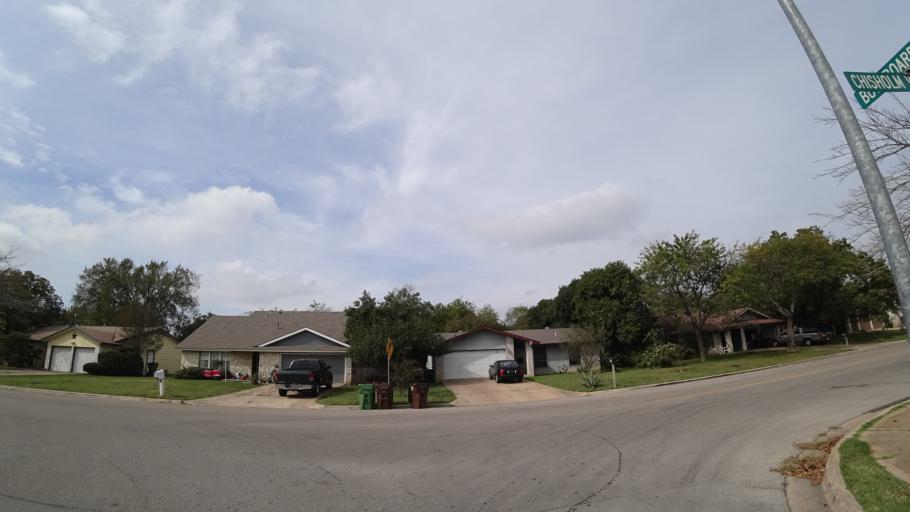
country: US
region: Texas
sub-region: Williamson County
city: Round Rock
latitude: 30.4939
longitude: -97.6853
